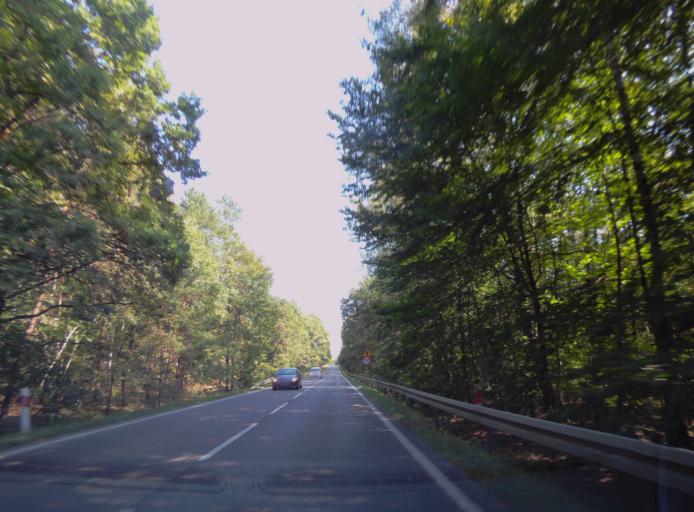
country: PL
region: Subcarpathian Voivodeship
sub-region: Powiat lezajski
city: Brzoza Krolewska
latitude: 50.2632
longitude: 22.3455
